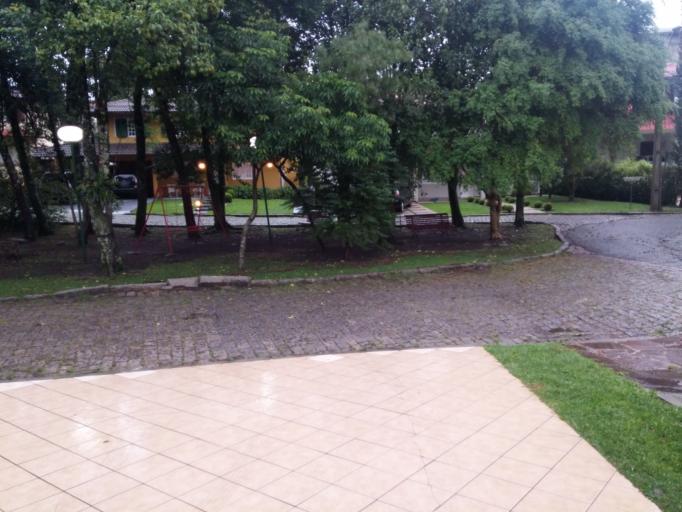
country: BR
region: Parana
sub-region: Curitiba
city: Curitiba
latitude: -25.4171
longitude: -49.3482
